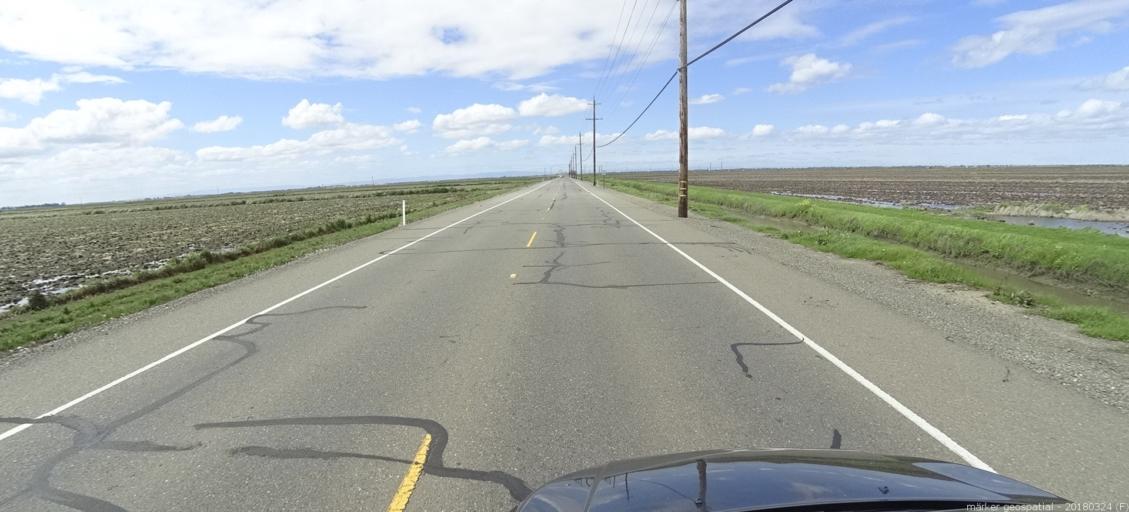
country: US
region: California
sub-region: Sacramento County
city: Elverta
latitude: 38.7143
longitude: -121.5241
